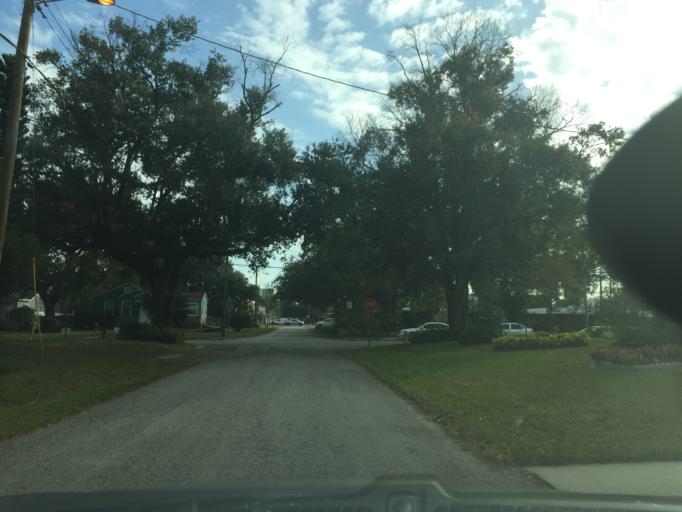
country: US
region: Florida
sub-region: Hillsborough County
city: Tampa
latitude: 27.9463
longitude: -82.4923
